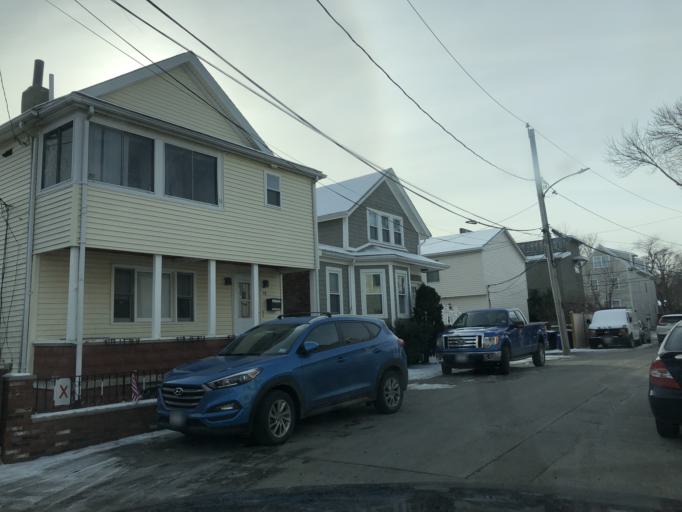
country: US
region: Massachusetts
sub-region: Middlesex County
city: Somerville
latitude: 42.3950
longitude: -71.1081
